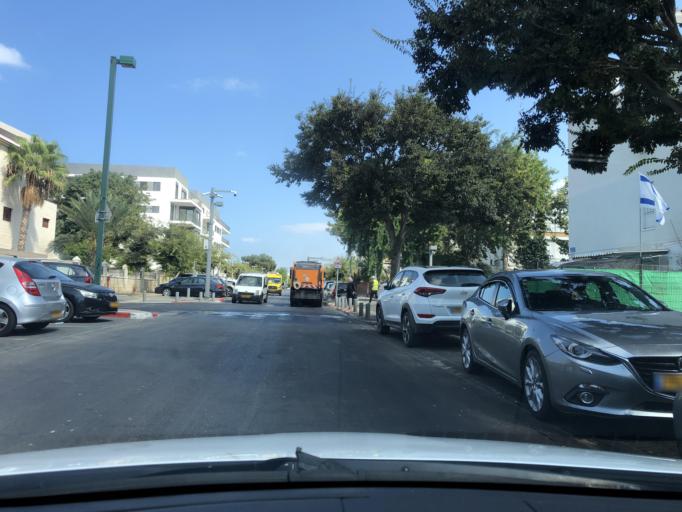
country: IL
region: Tel Aviv
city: Yafo
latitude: 32.0395
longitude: 34.7550
